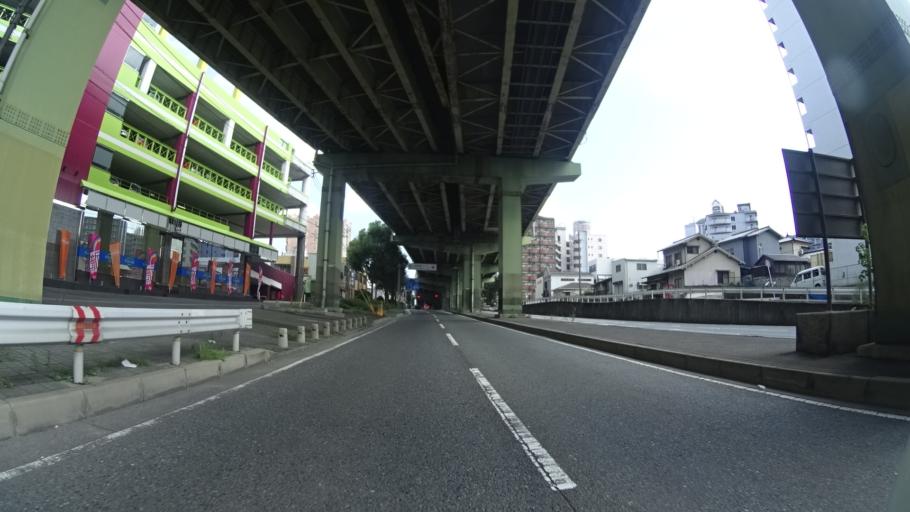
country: JP
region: Fukuoka
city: Kitakyushu
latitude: 33.8474
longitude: 130.8784
